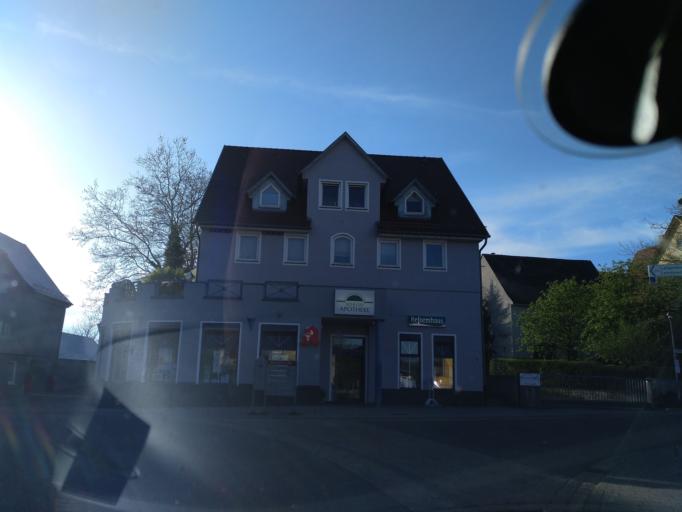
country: DE
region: Baden-Wuerttemberg
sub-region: Regierungsbezirk Stuttgart
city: Kirchberg an der Jagst
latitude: 49.2027
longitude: 9.9809
